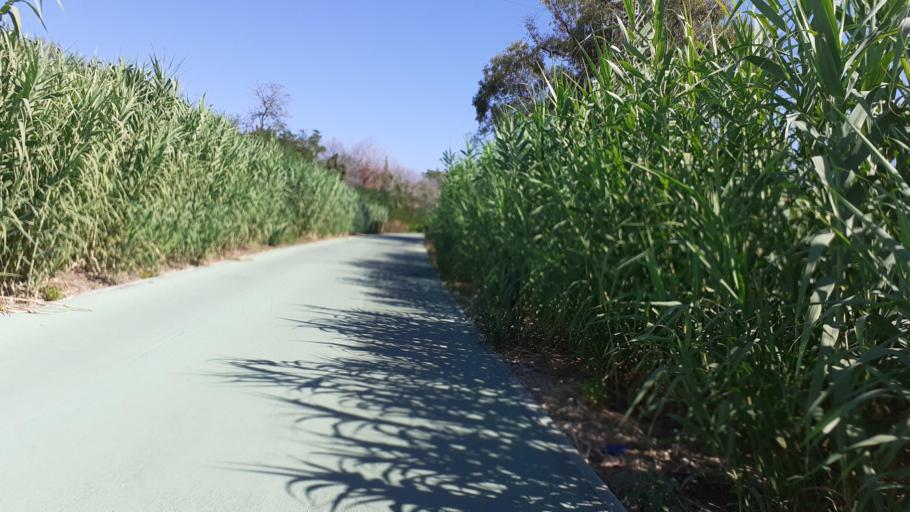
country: IT
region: Abruzzo
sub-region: Provincia di Chieti
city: Vasto
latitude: 42.1101
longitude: 14.7175
